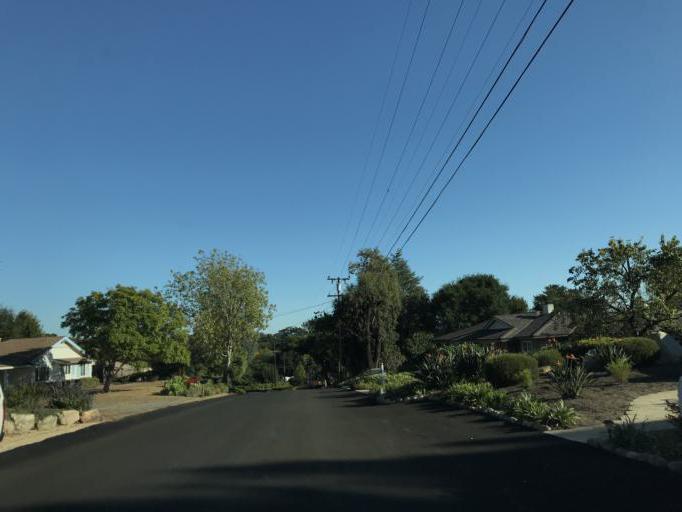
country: US
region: California
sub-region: Santa Barbara County
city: Goleta
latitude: 34.4604
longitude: -119.8176
